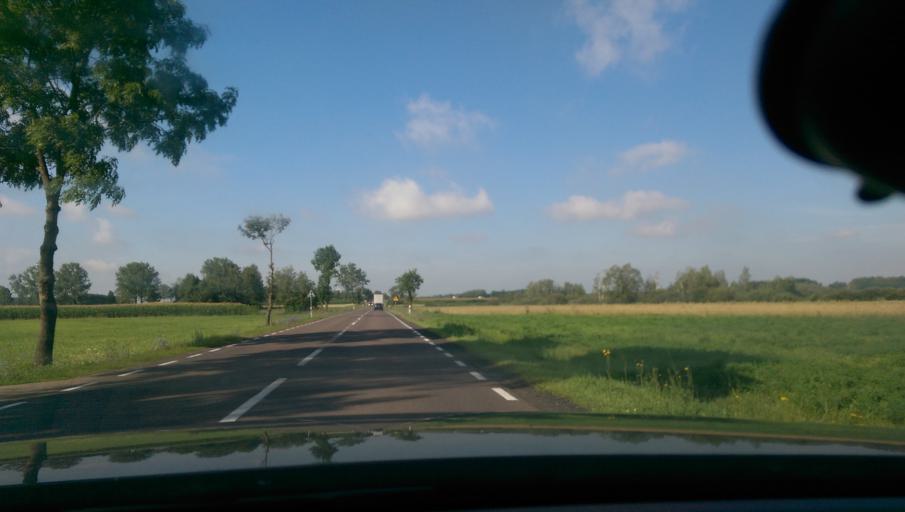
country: PL
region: Masovian Voivodeship
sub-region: Powiat plonski
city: Sochocin
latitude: 52.6672
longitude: 20.4517
